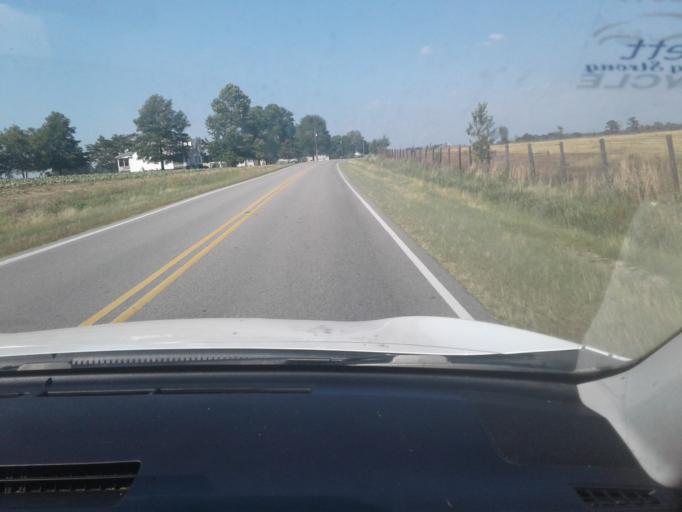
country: US
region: North Carolina
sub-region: Harnett County
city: Coats
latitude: 35.3722
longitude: -78.6294
